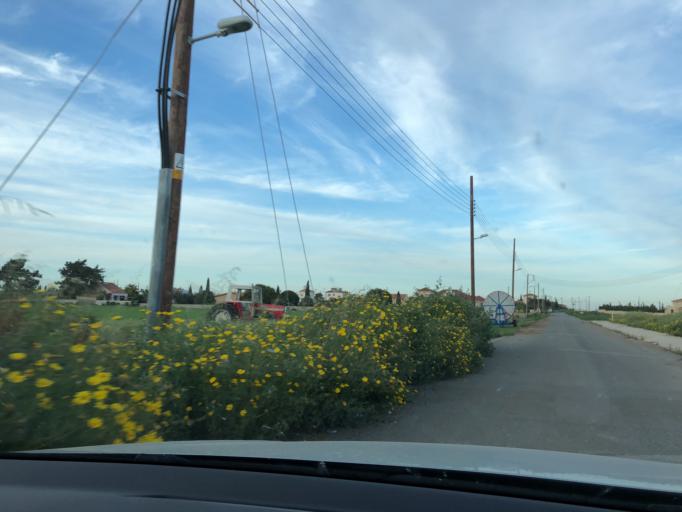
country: CY
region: Larnaka
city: Perivolia
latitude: 34.8361
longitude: 33.5985
